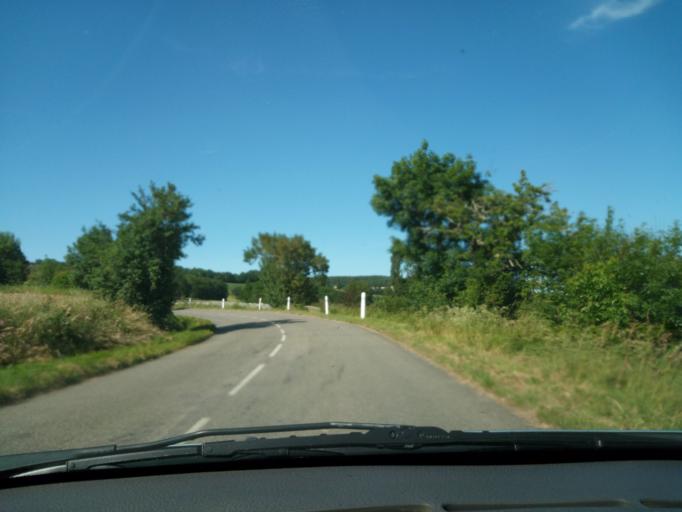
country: FR
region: Midi-Pyrenees
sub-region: Departement du Lot
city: Castelnau-Montratier
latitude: 44.2586
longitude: 1.3607
